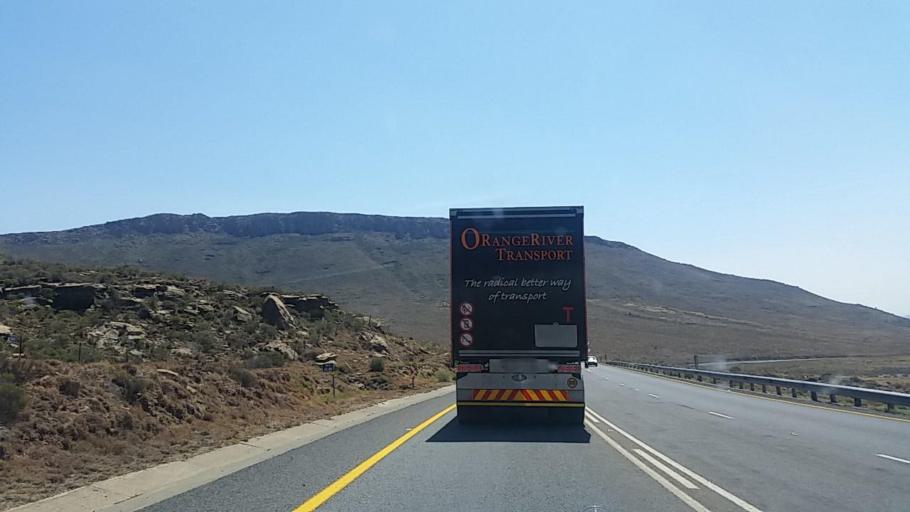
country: ZA
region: Eastern Cape
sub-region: Chris Hani District Municipality
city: Middelburg
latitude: -31.8231
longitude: 24.8558
